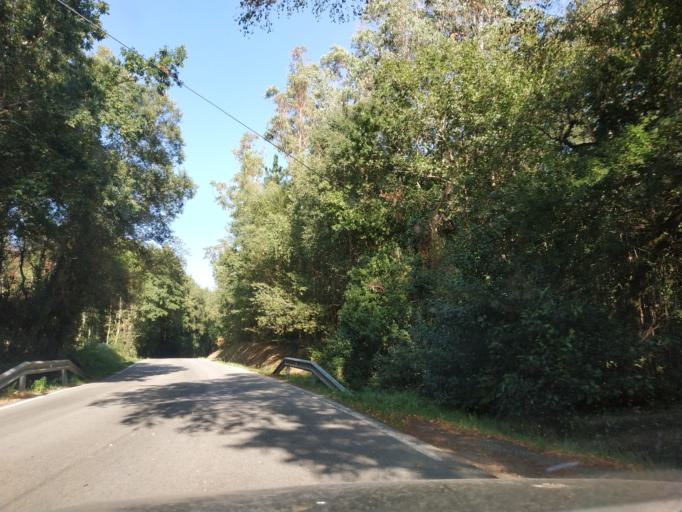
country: ES
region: Galicia
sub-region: Provincia da Coruna
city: Cerceda
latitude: 43.2335
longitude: -8.4737
